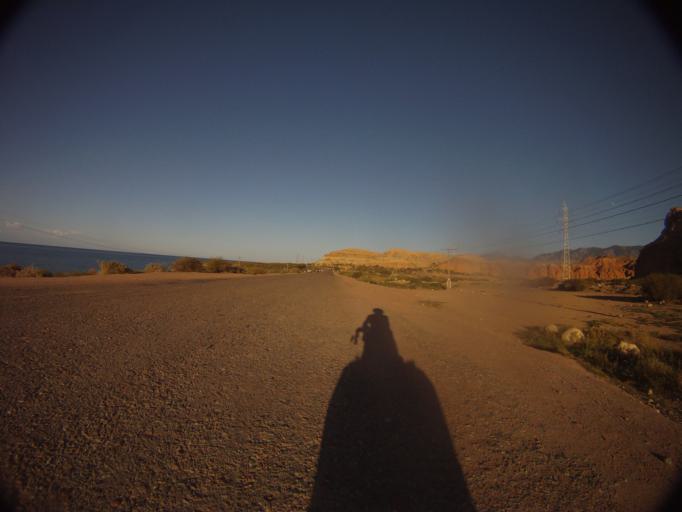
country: KG
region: Ysyk-Koel
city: Bokombayevskoye
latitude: 42.1556
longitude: 77.0583
